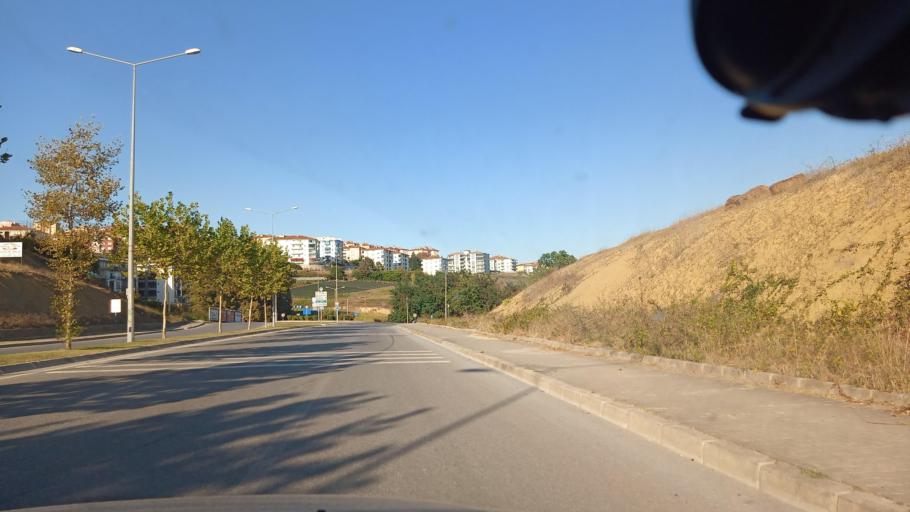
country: TR
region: Sakarya
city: Kazimpasa
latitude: 40.8527
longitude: 30.2878
